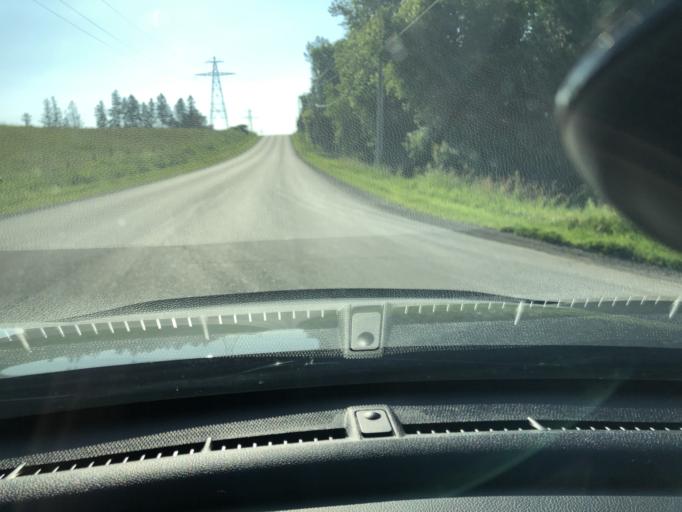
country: CA
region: Ontario
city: Stratford
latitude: 43.3884
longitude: -80.8877
